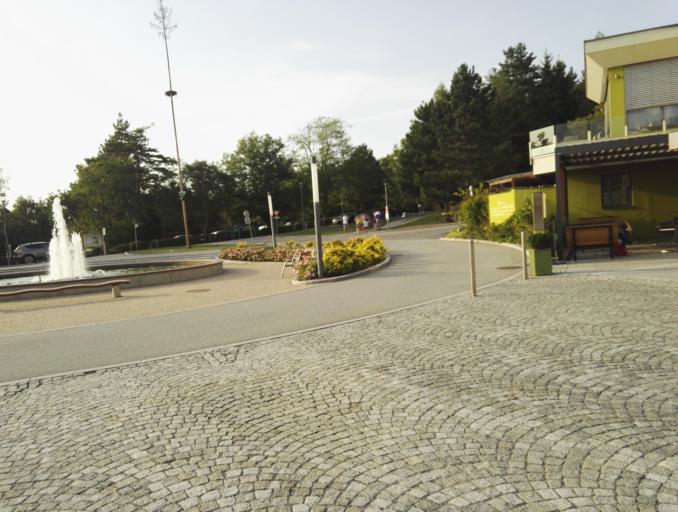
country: AT
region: Styria
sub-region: Politischer Bezirk Hartberg-Fuerstenfeld
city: Loipersdorf bei Fuerstenfeld
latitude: 46.9852
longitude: 16.1107
